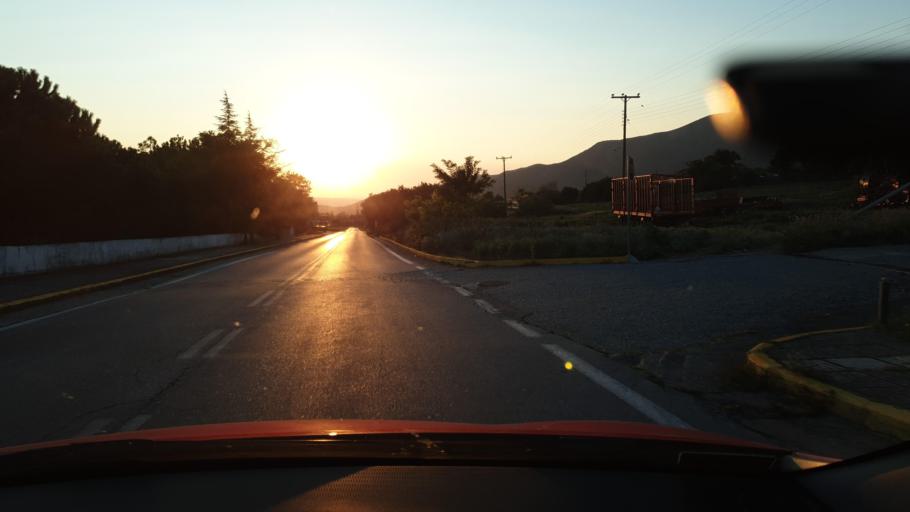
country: GR
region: Central Macedonia
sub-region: Nomos Chalkidikis
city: Galatista
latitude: 40.4677
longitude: 23.2691
